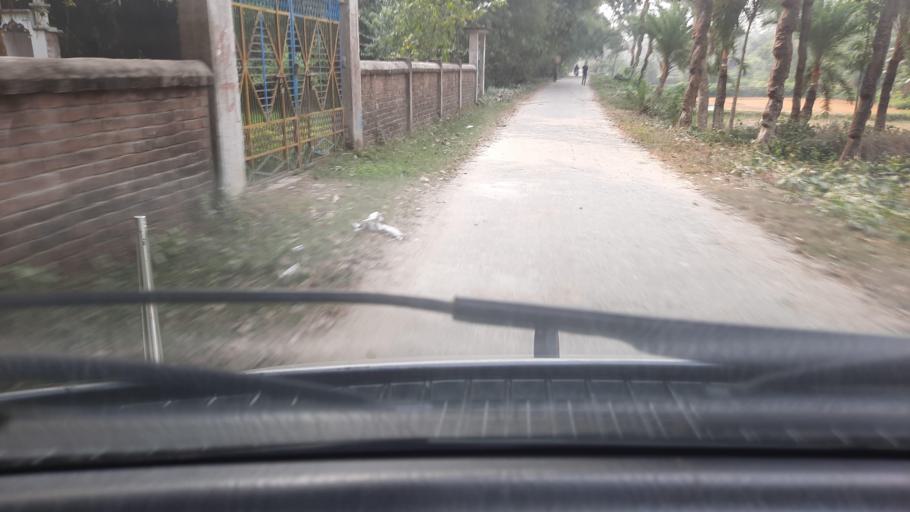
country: BD
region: Khulna
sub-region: Chuadanga
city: Nowlamary
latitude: 23.5996
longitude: 88.8447
